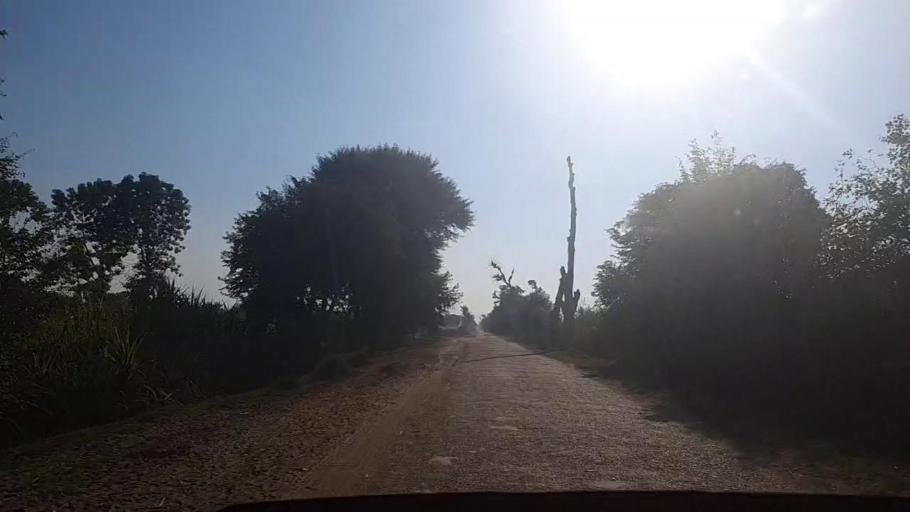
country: PK
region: Sindh
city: Gambat
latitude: 27.3611
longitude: 68.4578
